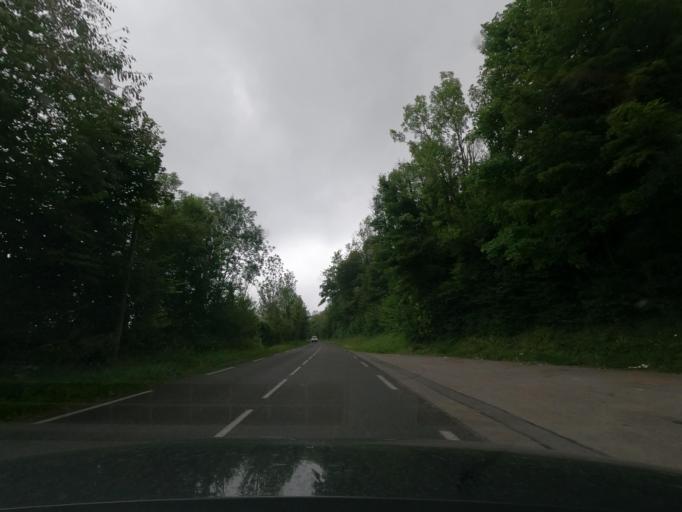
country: FR
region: Haute-Normandie
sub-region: Departement de la Seine-Maritime
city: Gaillefontaine
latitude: 49.6556
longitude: 1.6269
